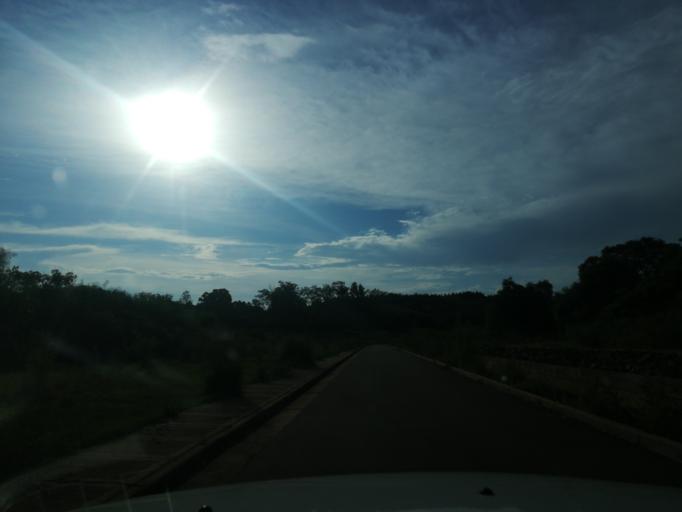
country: AR
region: Misiones
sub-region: Departamento de Candelaria
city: Candelaria
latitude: -27.4541
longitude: -55.7719
